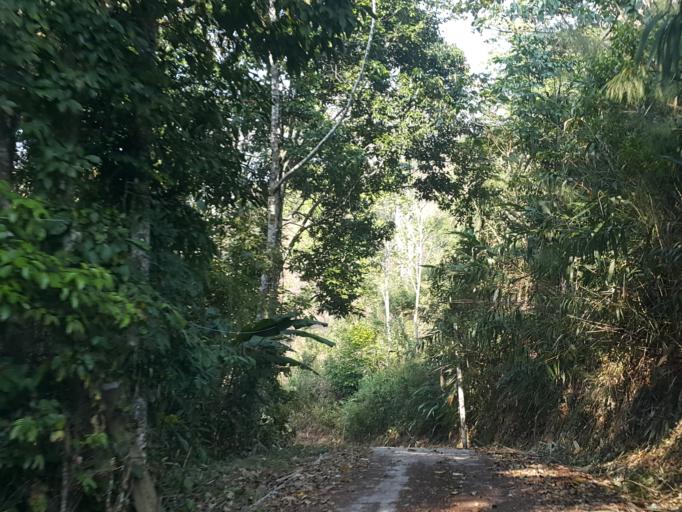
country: TH
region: Chiang Mai
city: Samoeng
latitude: 19.0147
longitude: 98.7597
